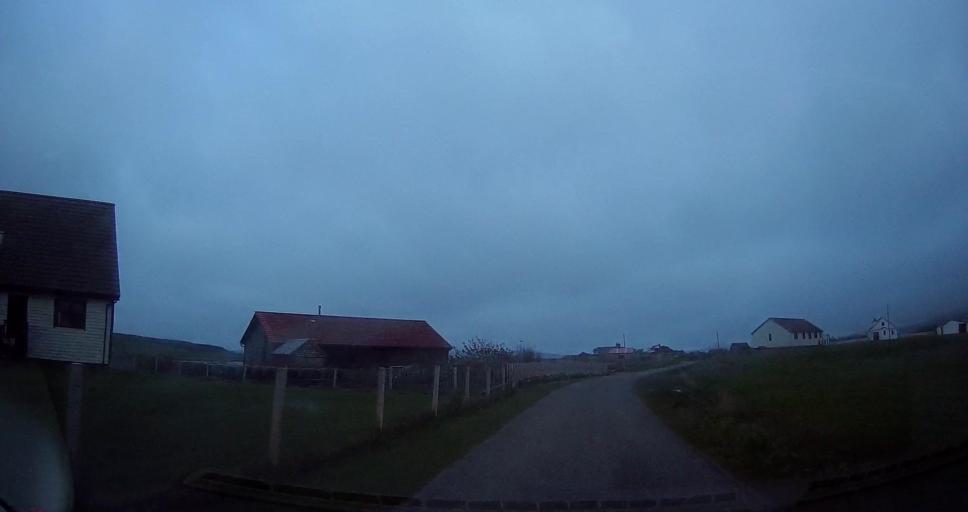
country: GB
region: Scotland
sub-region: Shetland Islands
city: Sandwick
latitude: 60.0404
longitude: -1.2186
